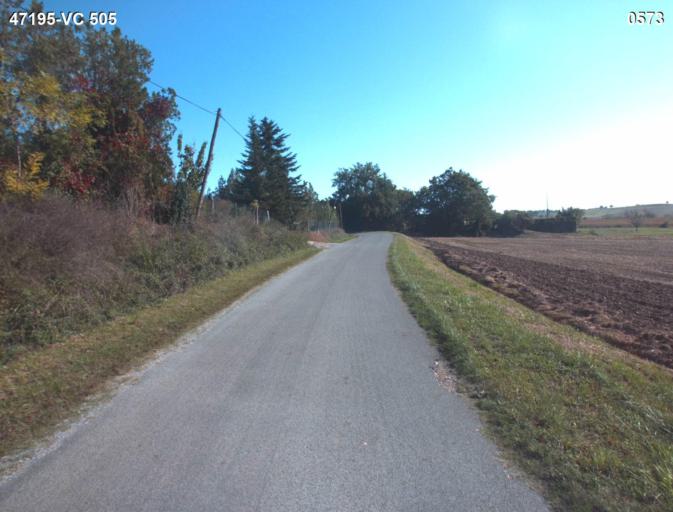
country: FR
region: Aquitaine
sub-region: Departement du Lot-et-Garonne
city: Nerac
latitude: 44.1425
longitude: 0.3673
